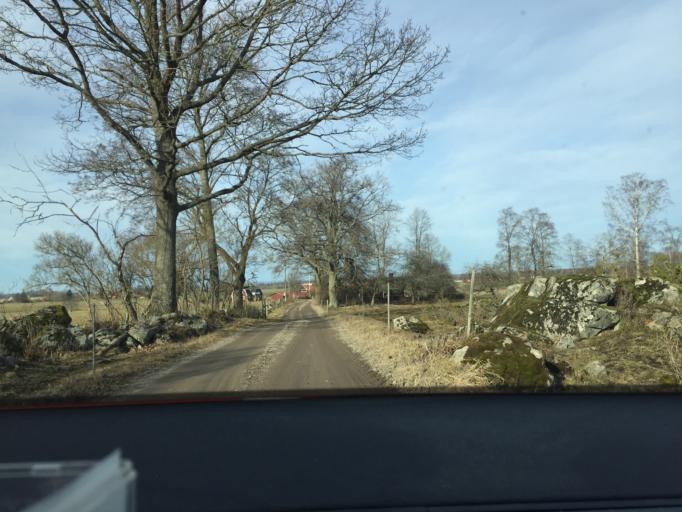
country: SE
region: OErebro
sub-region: Hallsbergs Kommun
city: Skollersta
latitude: 59.1232
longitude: 15.4340
